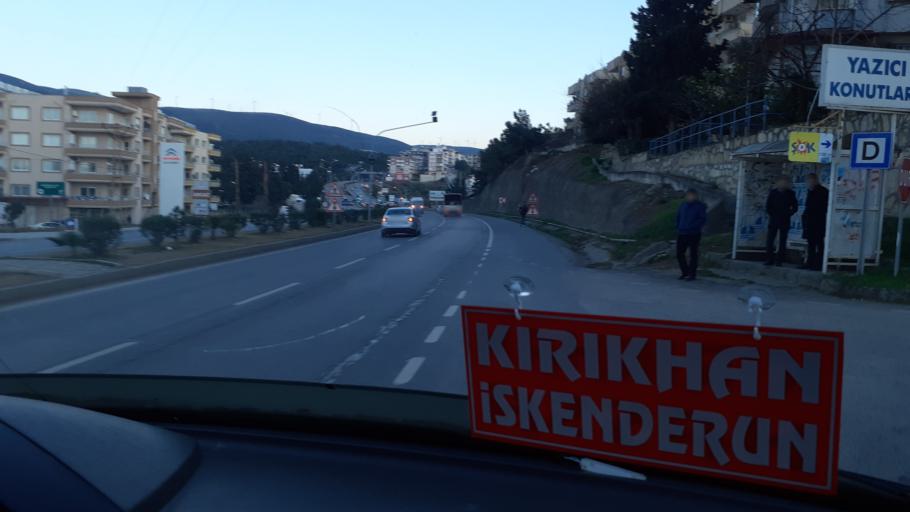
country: TR
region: Hatay
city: Cirtiman
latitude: 36.5301
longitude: 36.1520
